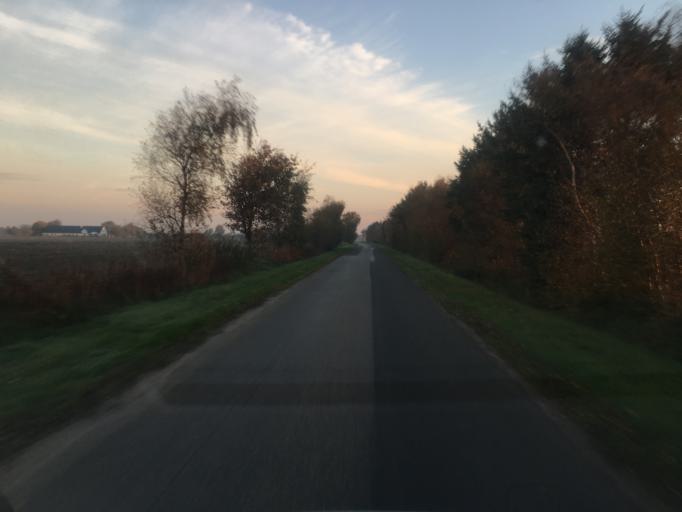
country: DK
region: South Denmark
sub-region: Tonder Kommune
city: Logumkloster
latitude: 55.0589
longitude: 9.0237
